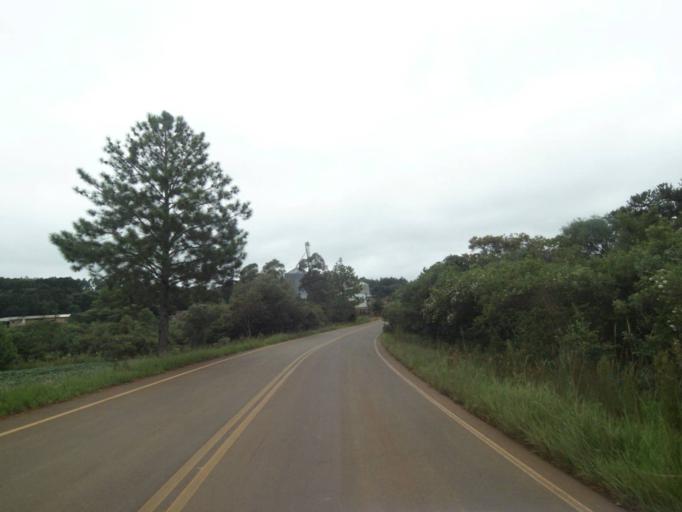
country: BR
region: Parana
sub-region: Pitanga
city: Pitanga
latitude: -24.9327
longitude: -51.8822
